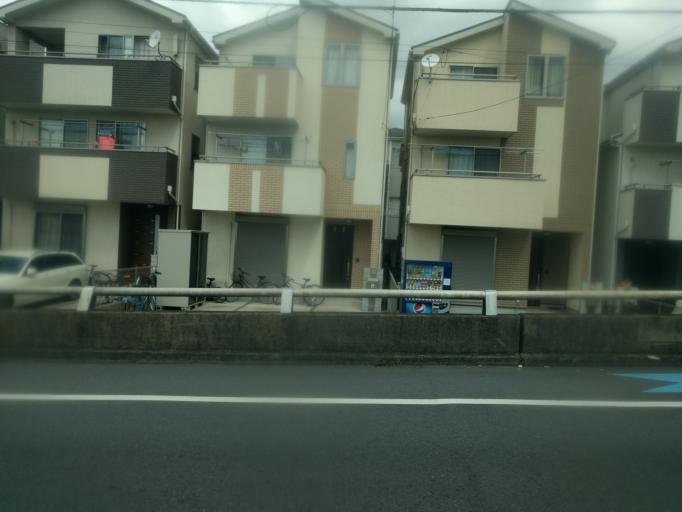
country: JP
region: Saitama
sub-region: Kawaguchi-shi
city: Hatogaya-honcho
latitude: 35.8248
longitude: 139.7253
